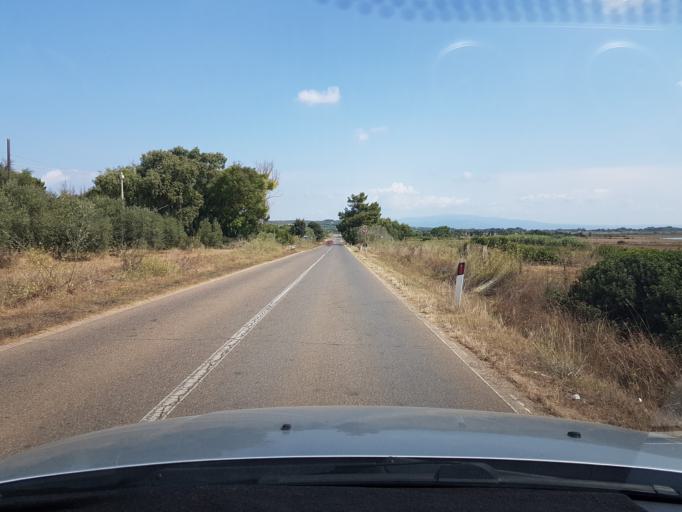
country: IT
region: Sardinia
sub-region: Provincia di Oristano
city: Cabras
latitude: 39.9005
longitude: 8.4354
